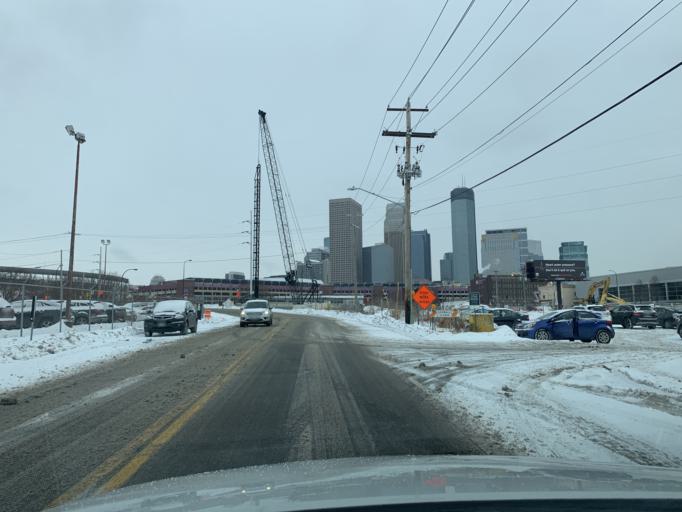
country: US
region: Minnesota
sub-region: Hennepin County
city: Minneapolis
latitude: 44.9799
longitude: -93.2841
